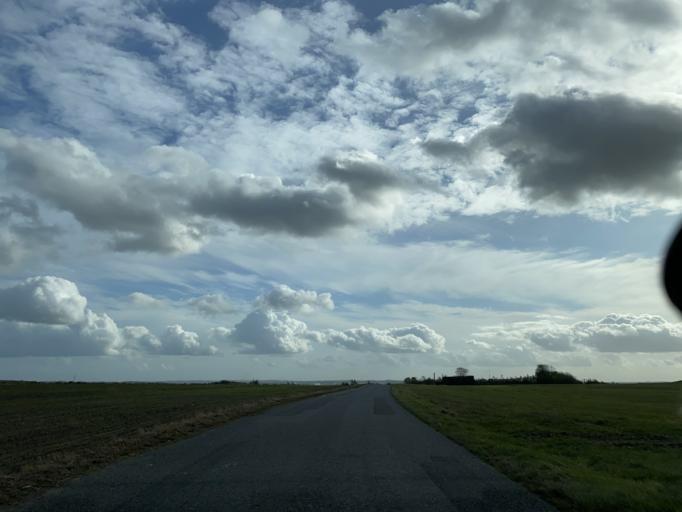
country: DK
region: Central Jutland
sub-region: Arhus Kommune
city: Sabro
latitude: 56.2041
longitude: 9.9934
